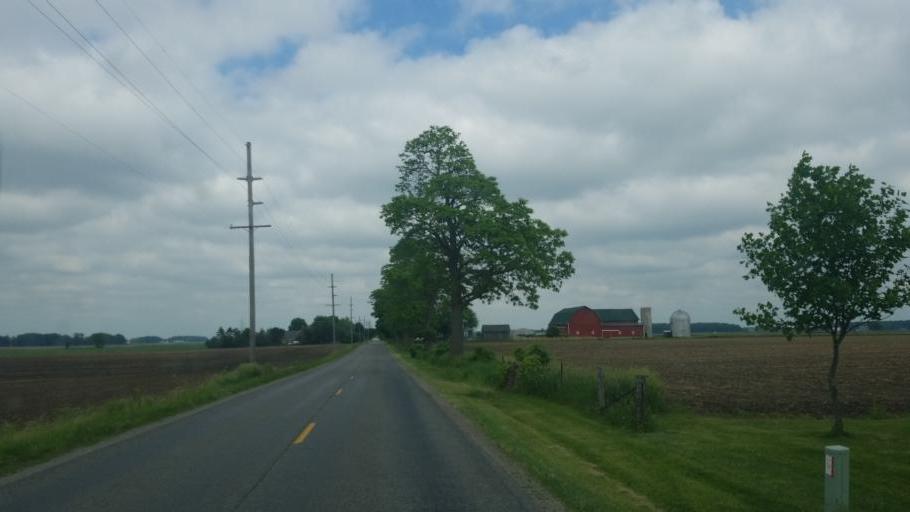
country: US
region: Indiana
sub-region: Elkhart County
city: Wakarusa
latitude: 41.4935
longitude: -86.0161
